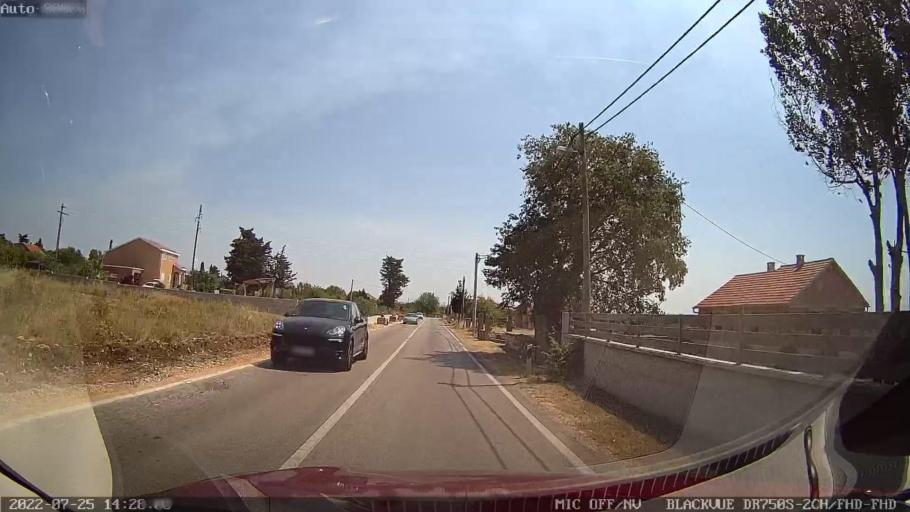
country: HR
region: Zadarska
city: Policnik
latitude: 44.1282
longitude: 15.3479
